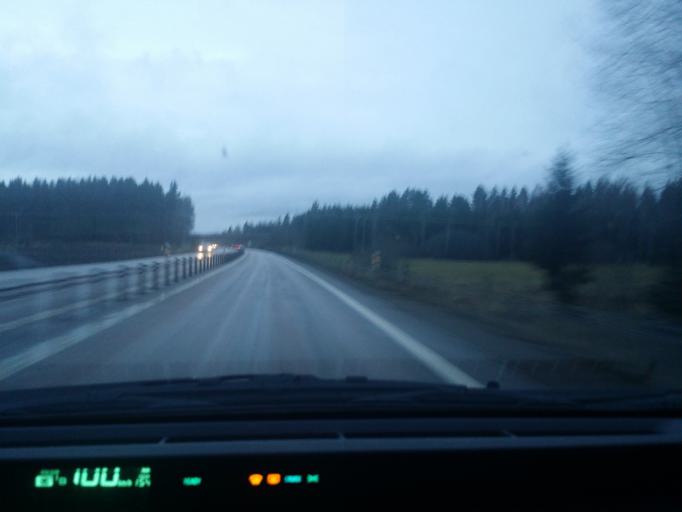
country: SE
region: Soedermanland
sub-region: Eskilstuna Kommun
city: Kvicksund
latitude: 59.4305
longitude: 16.3625
